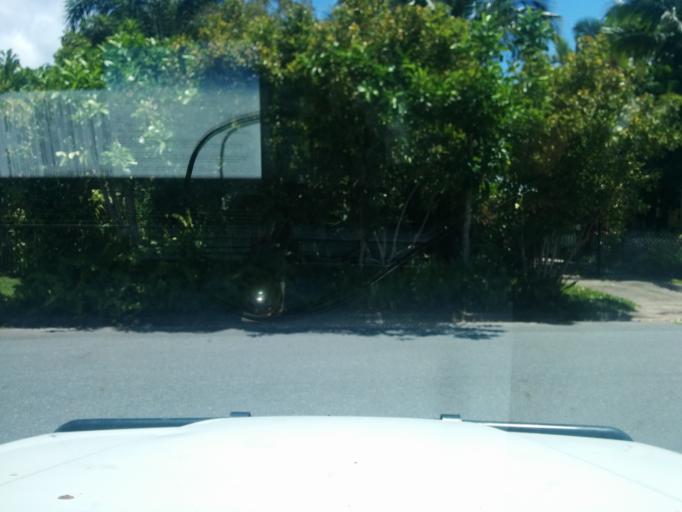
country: AU
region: Queensland
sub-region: Cairns
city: Cairns
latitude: -16.9016
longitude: 145.7458
